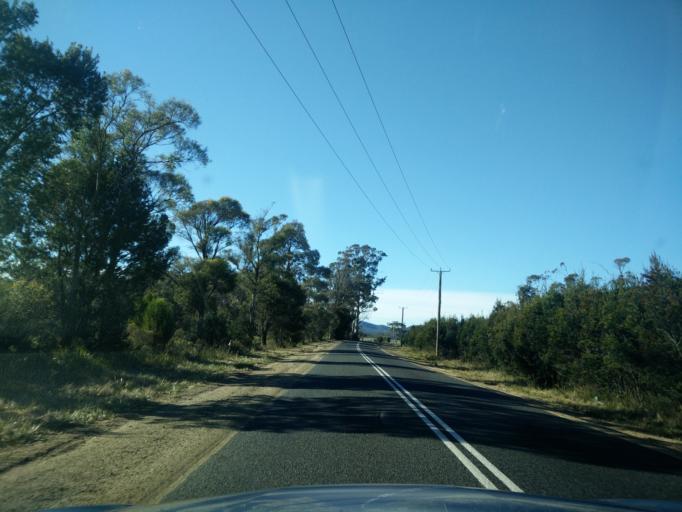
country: AU
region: Tasmania
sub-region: Break O'Day
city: St Helens
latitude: -41.8982
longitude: 148.2549
